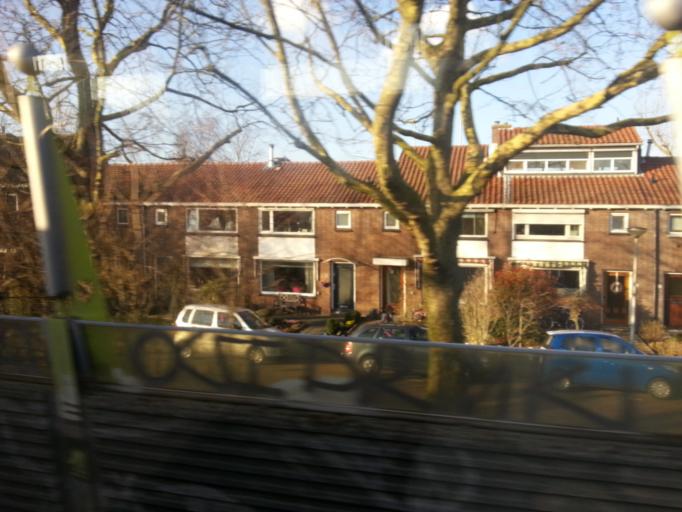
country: NL
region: South Holland
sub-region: Gemeente Gouda
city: Gouda
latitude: 52.0168
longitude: 4.7144
